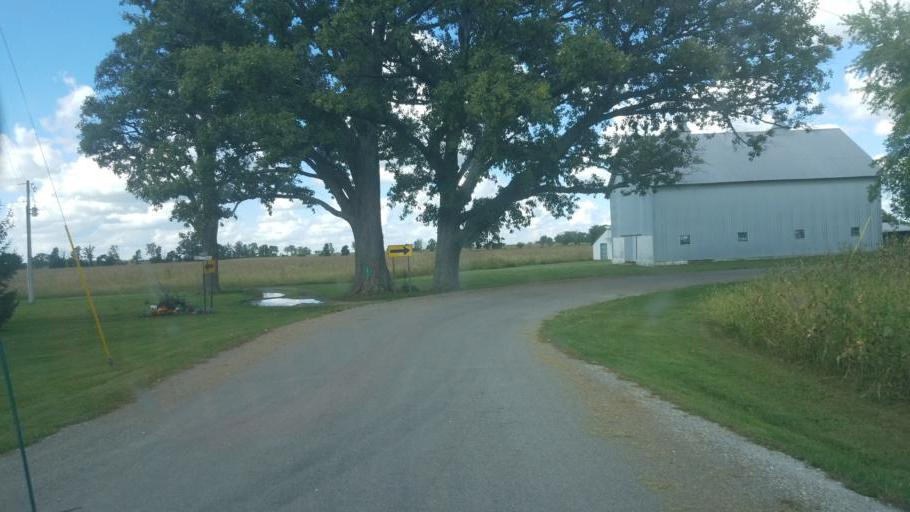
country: US
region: Ohio
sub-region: Hardin County
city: Kenton
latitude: 40.5482
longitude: -83.5448
